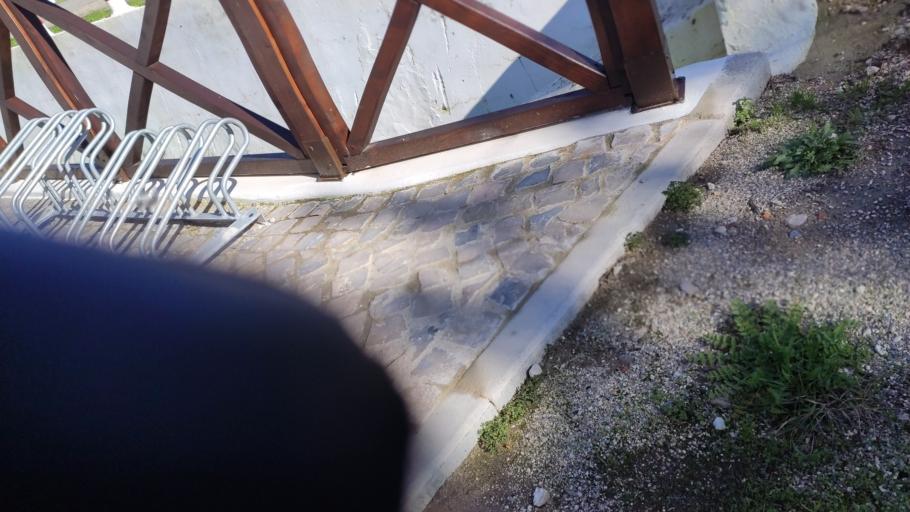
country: PT
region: Faro
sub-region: Sao Bras de Alportel
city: Sao Bras de Alportel
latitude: 37.1528
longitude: -7.8562
